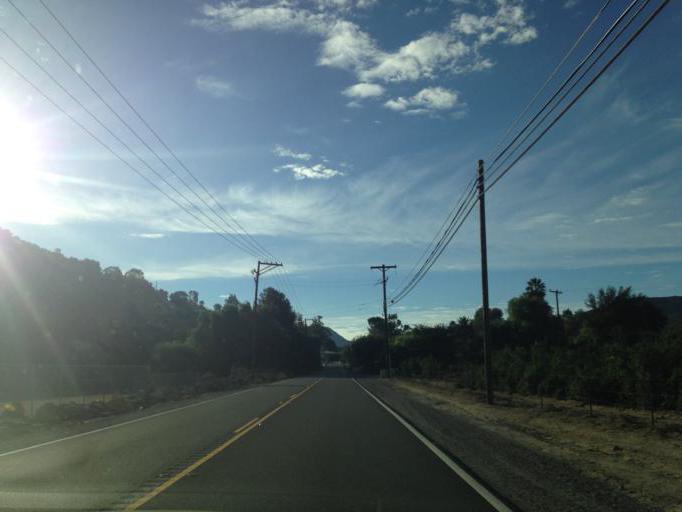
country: US
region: California
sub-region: San Diego County
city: Valley Center
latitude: 33.2935
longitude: -116.9693
